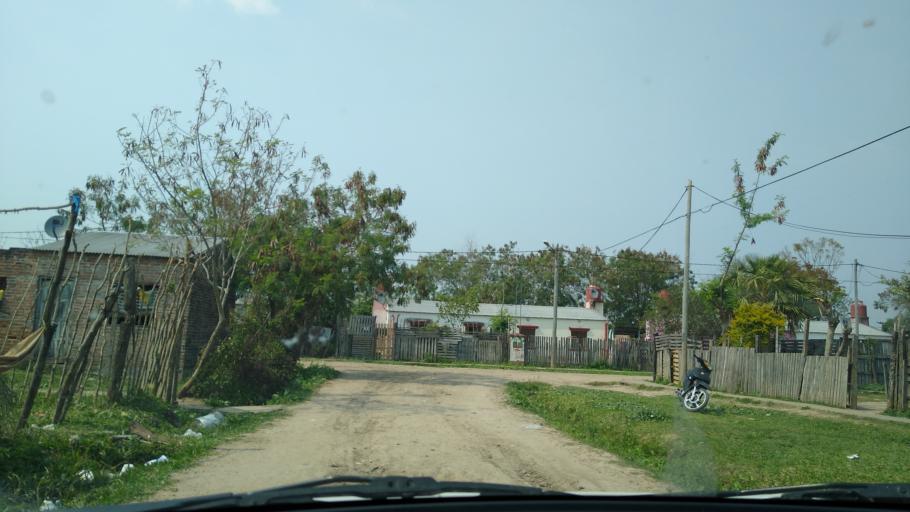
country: AR
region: Chaco
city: Fontana
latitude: -27.3989
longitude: -58.9867
